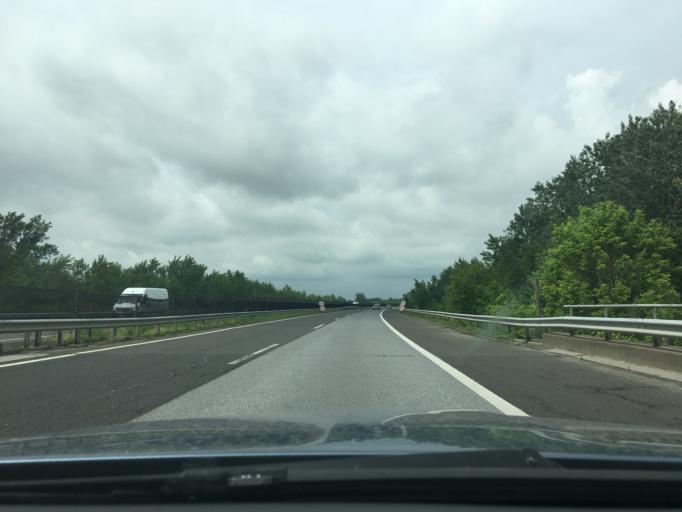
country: HU
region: Hajdu-Bihar
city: Polgar
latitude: 47.8497
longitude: 21.0648
